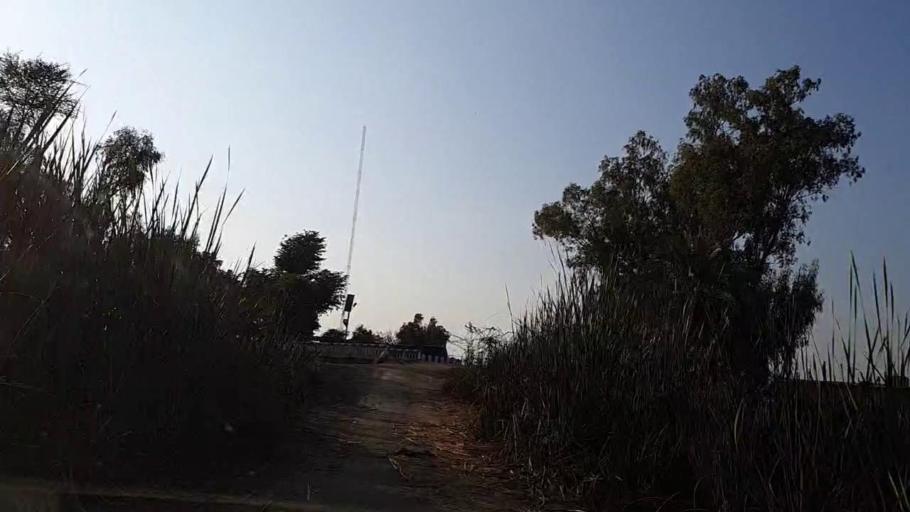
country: PK
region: Sindh
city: Sakrand
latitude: 26.0940
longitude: 68.3736
